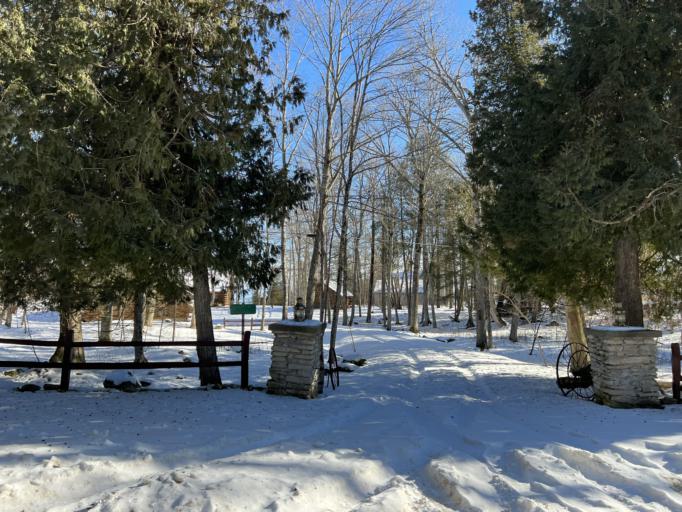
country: US
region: Michigan
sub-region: Delta County
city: Escanaba
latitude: 45.3434
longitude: -86.8682
